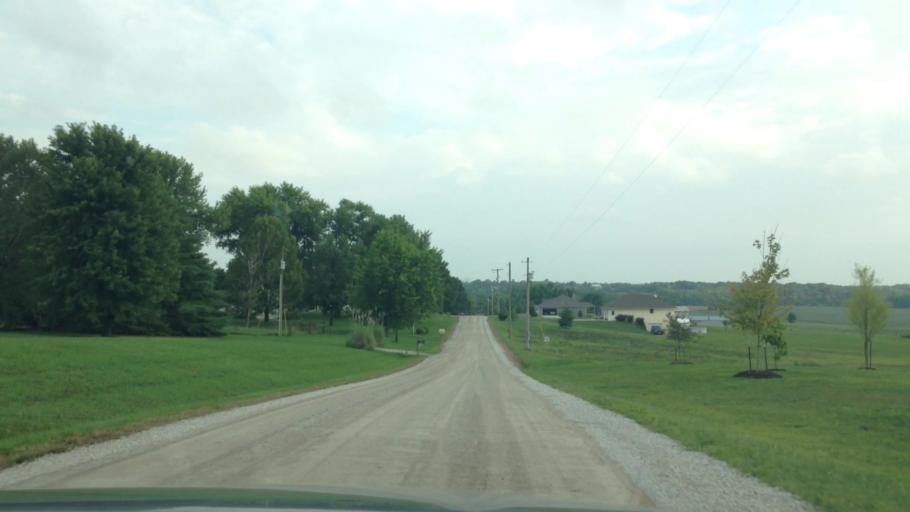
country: US
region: Missouri
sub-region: Clay County
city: Smithville
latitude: 39.4026
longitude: -94.6435
